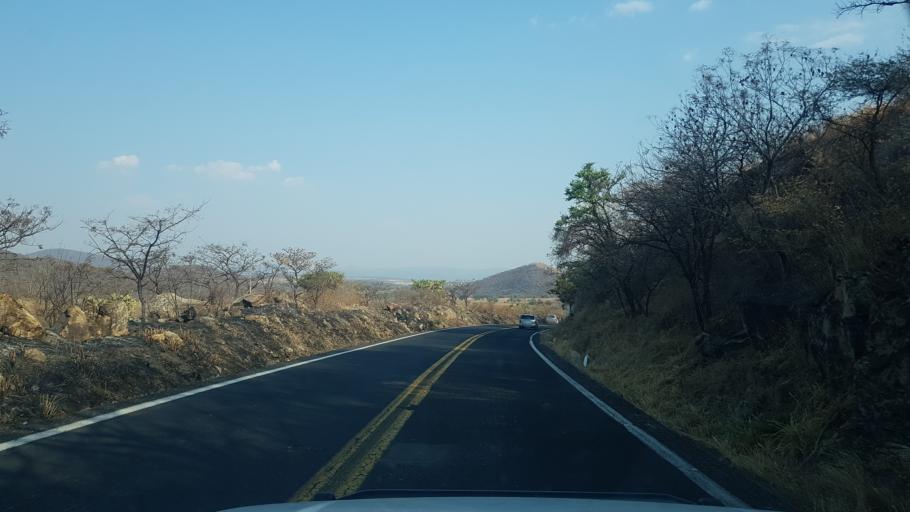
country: MX
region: Puebla
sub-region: Tilapa
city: San Felix Rijo
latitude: 18.6398
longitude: -98.5885
